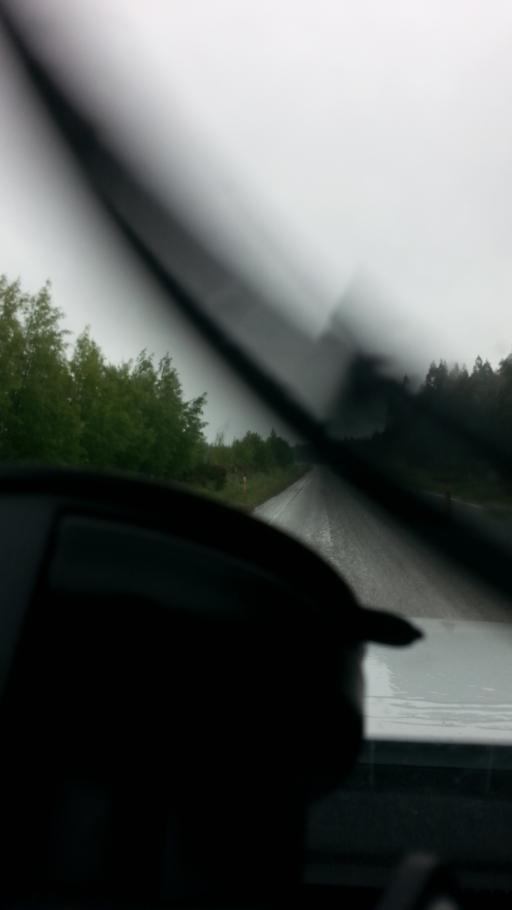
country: NZ
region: Wellington
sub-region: Masterton District
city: Masterton
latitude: -40.8055
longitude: 175.6197
